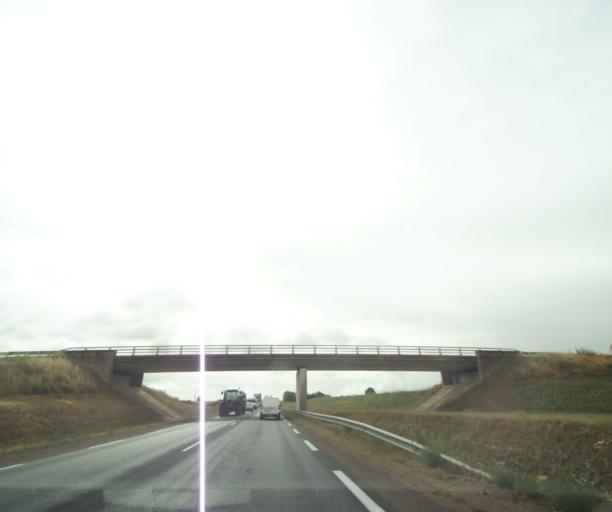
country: FR
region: Pays de la Loire
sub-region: Departement de la Vendee
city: Lucon
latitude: 46.4722
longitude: -1.1674
